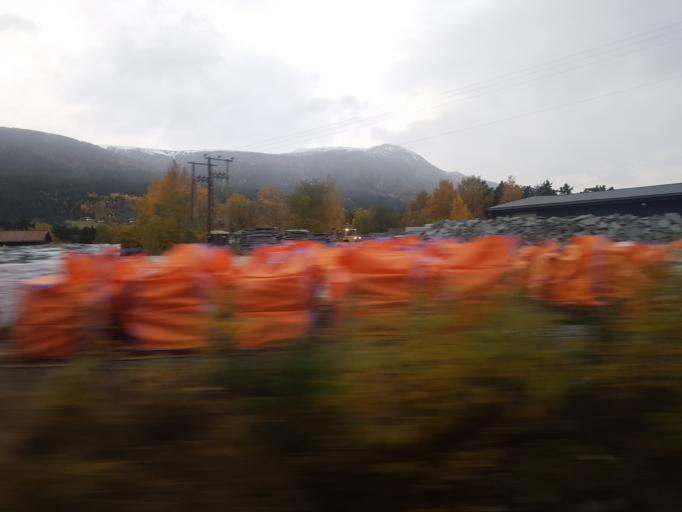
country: NO
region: Oppland
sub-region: Dovre
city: Dovre
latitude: 61.9925
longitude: 9.2374
